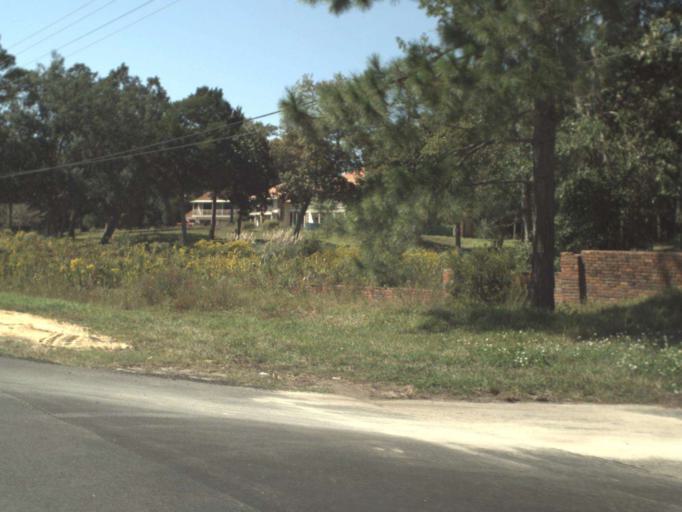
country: US
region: Florida
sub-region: Walton County
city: Miramar Beach
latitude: 30.4738
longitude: -86.3371
